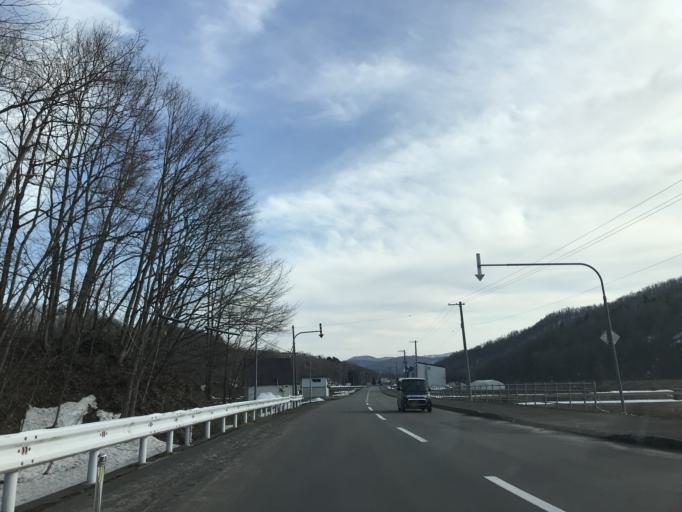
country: JP
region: Hokkaido
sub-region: Asahikawa-shi
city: Asahikawa
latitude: 43.7297
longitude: 142.3208
